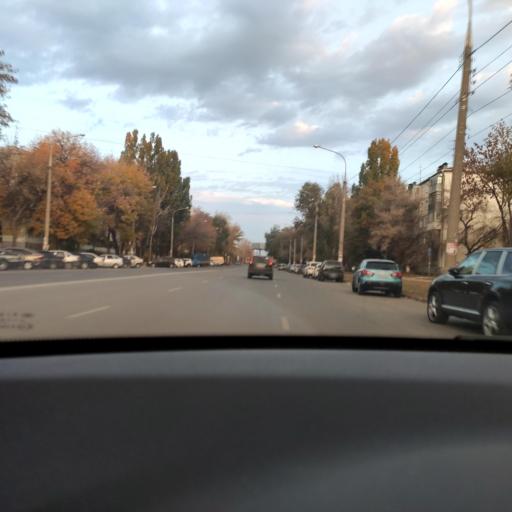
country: RU
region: Samara
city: Samara
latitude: 53.2264
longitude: 50.2102
